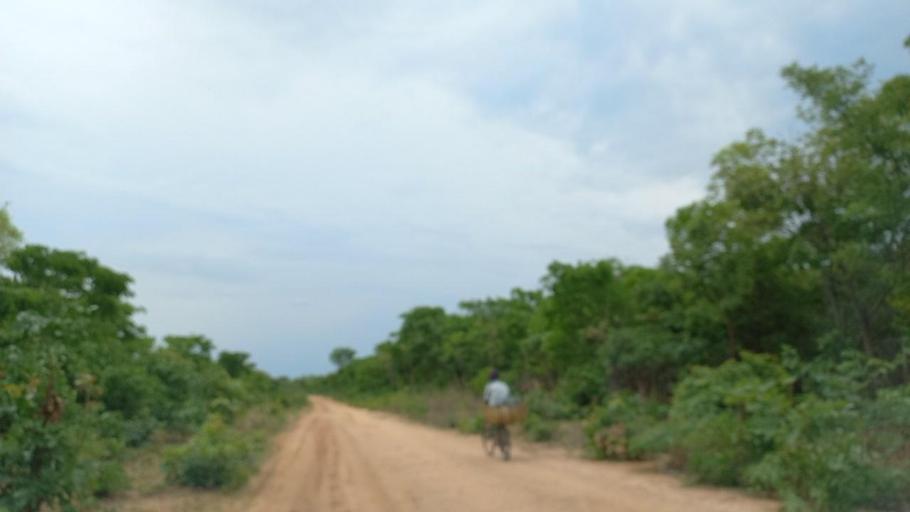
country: ZM
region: North-Western
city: Mufumbwe
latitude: -13.6509
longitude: 24.9788
